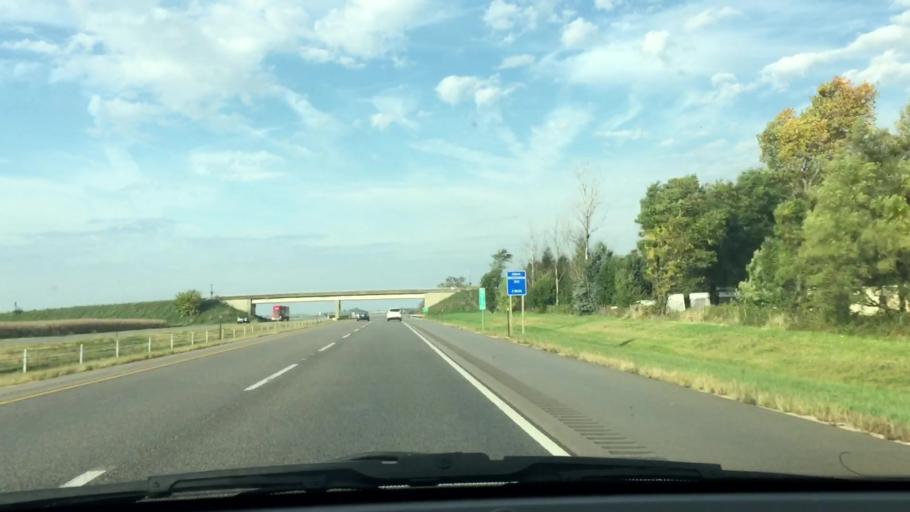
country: US
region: Illinois
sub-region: Ogle County
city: Rochelle
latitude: 41.8869
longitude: -89.1096
